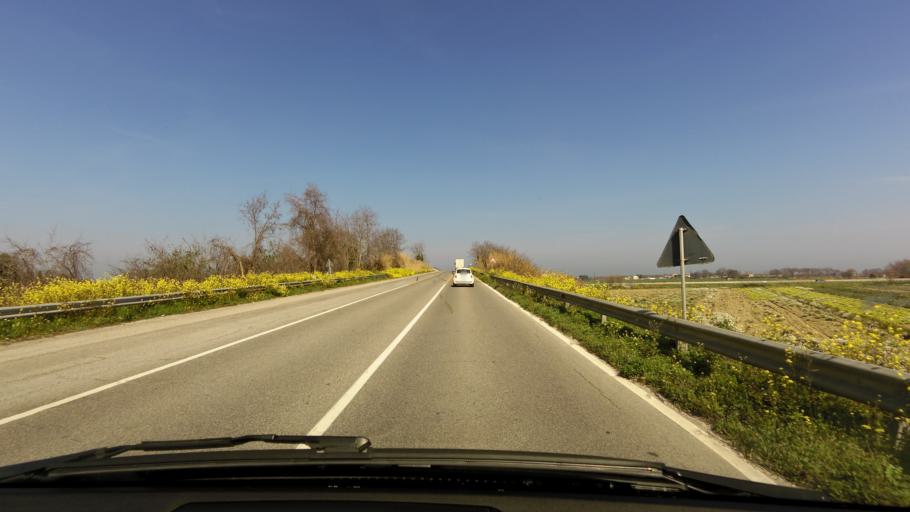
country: IT
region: The Marches
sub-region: Provincia di Macerata
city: Porto Recanati
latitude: 43.4023
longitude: 13.6621
